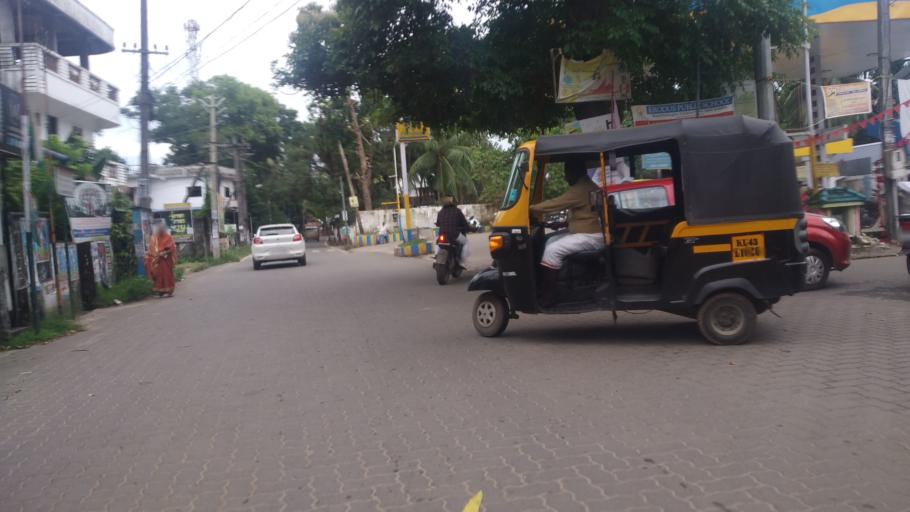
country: IN
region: Kerala
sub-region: Alappuzha
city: Arukutti
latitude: 9.8615
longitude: 76.2922
